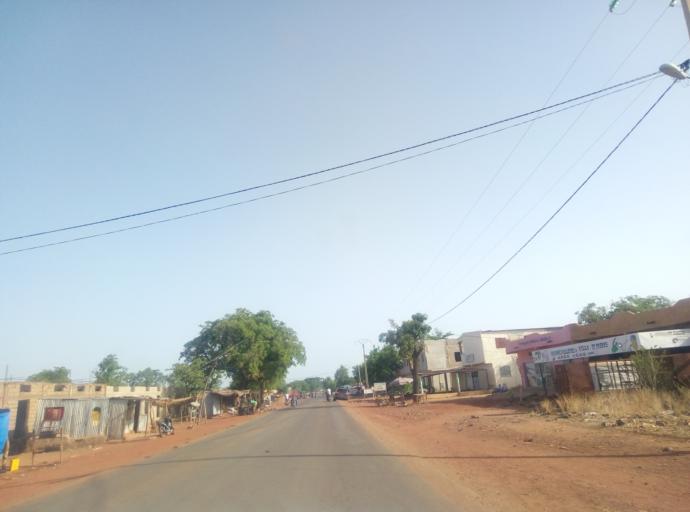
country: ML
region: Bamako
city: Bamako
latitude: 12.5960
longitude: -7.7667
